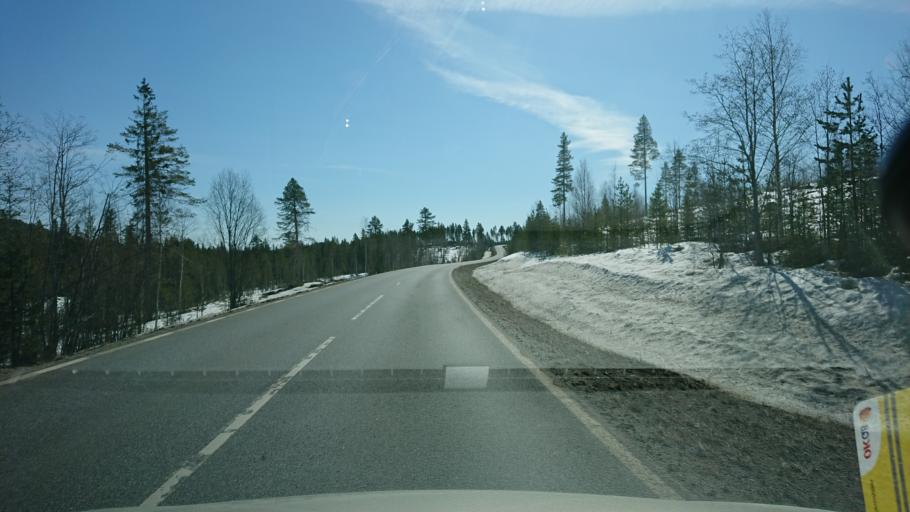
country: SE
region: Vaesterbotten
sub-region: Dorotea Kommun
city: Dorotea
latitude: 64.0236
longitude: 16.2816
